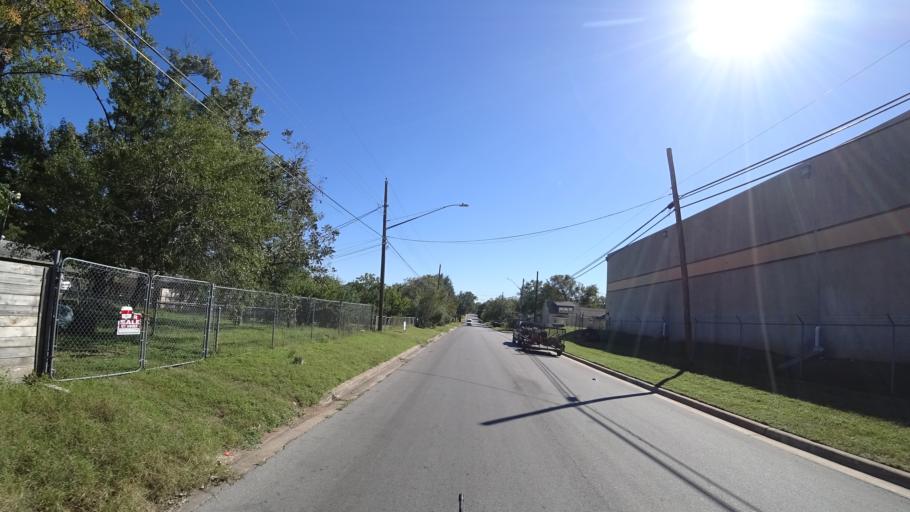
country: US
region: Texas
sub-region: Travis County
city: Austin
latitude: 30.2819
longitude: -97.7015
